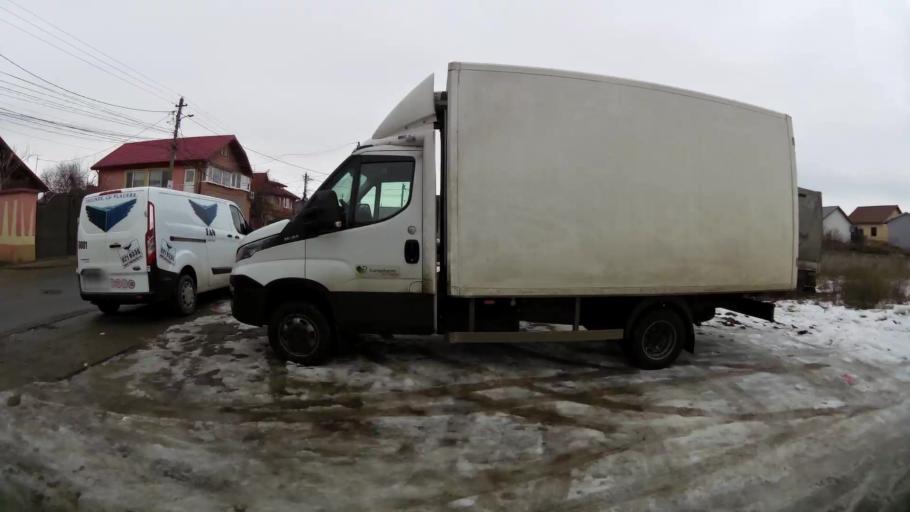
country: RO
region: Ilfov
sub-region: Comuna Pantelimon
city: Pantelimon
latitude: 44.4578
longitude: 26.2155
